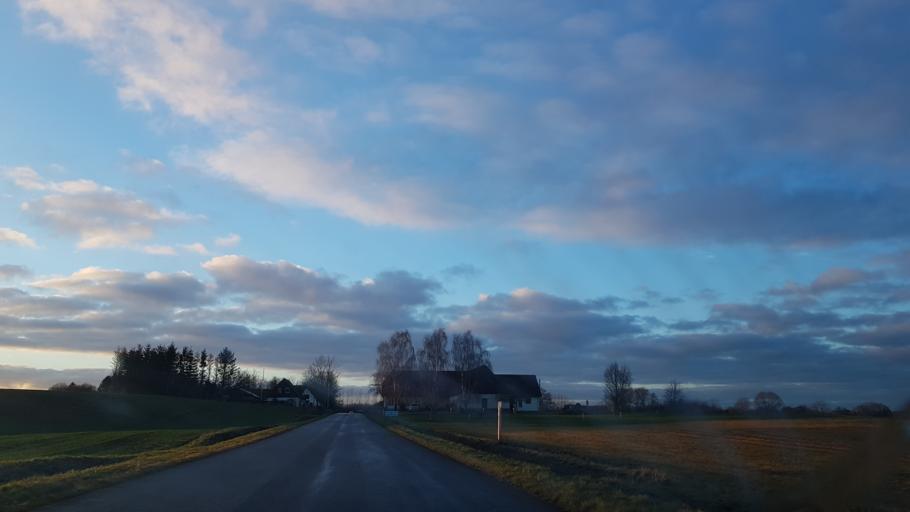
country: DK
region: South Denmark
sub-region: Kolding Kommune
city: Vamdrup
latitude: 55.3751
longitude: 9.2842
